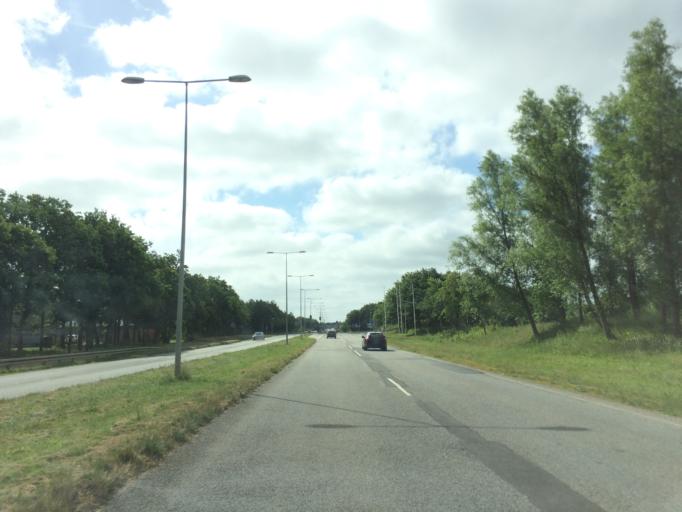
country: DK
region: Central Jutland
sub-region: Herning Kommune
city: Herning
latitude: 56.1466
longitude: 8.9378
